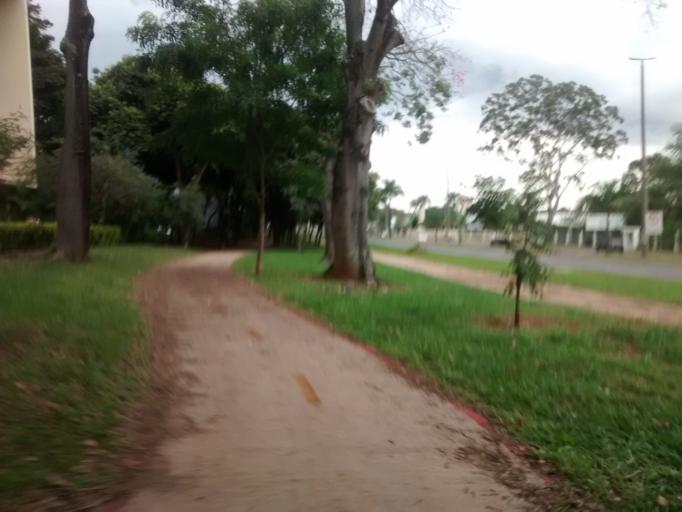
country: BR
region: Federal District
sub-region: Brasilia
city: Brasilia
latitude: -15.7638
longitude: -47.8769
